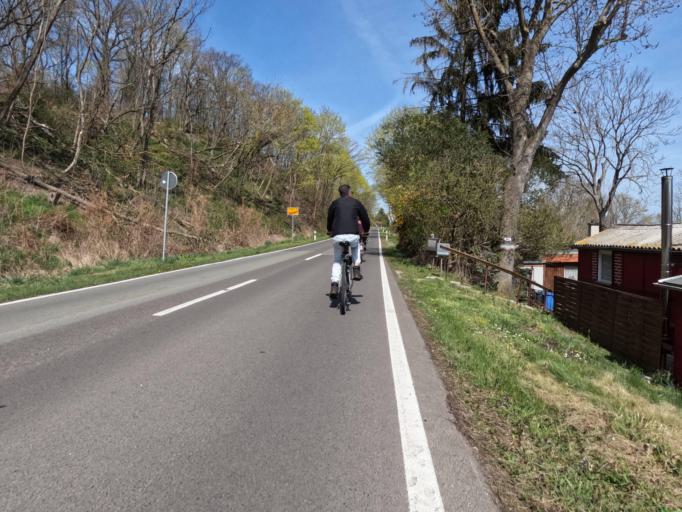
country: DE
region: Saxony-Anhalt
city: Beesenstedt
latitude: 51.5900
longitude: 11.7549
